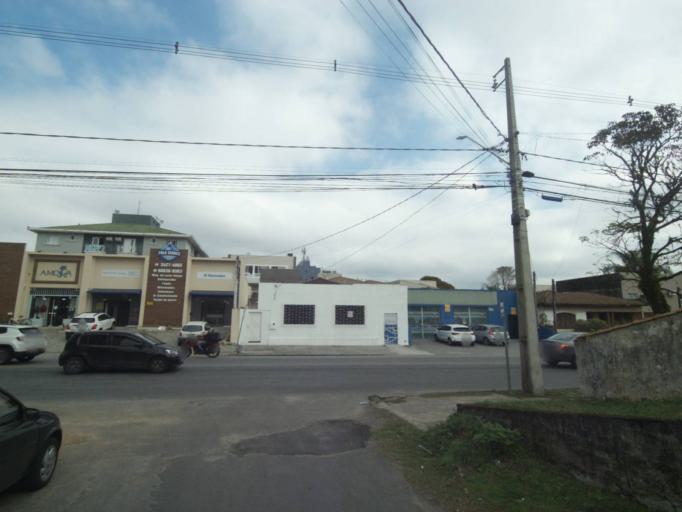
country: BR
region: Parana
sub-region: Paranagua
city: Paranagua
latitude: -25.5229
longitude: -48.5153
